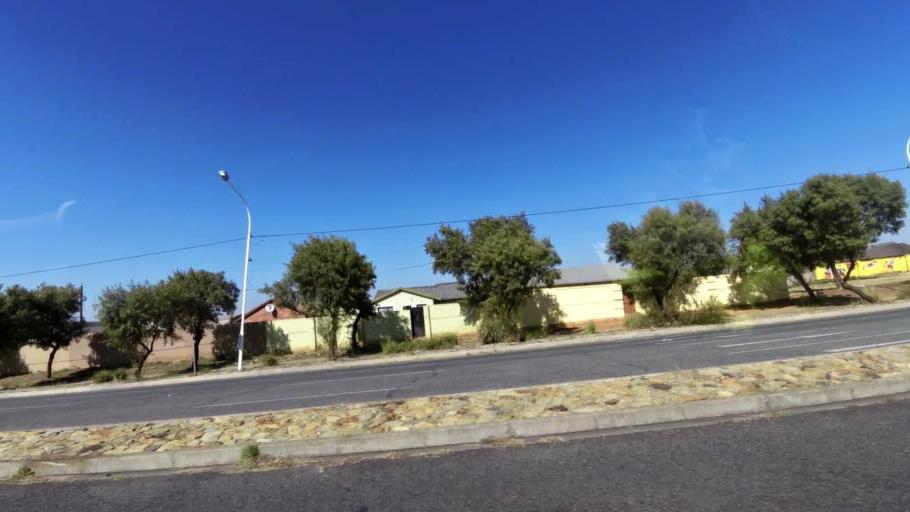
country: ZA
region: Gauteng
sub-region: City of Johannesburg Metropolitan Municipality
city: Johannesburg
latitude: -26.2469
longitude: 27.9829
